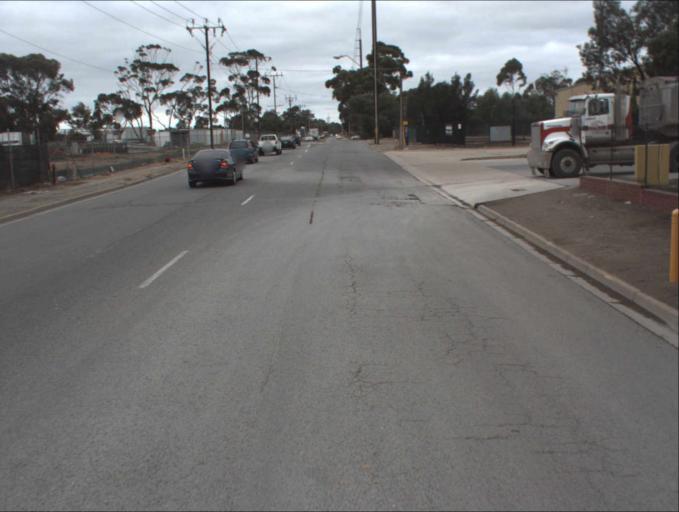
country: AU
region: South Australia
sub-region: Port Adelaide Enfield
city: Enfield
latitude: -34.8336
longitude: 138.5918
